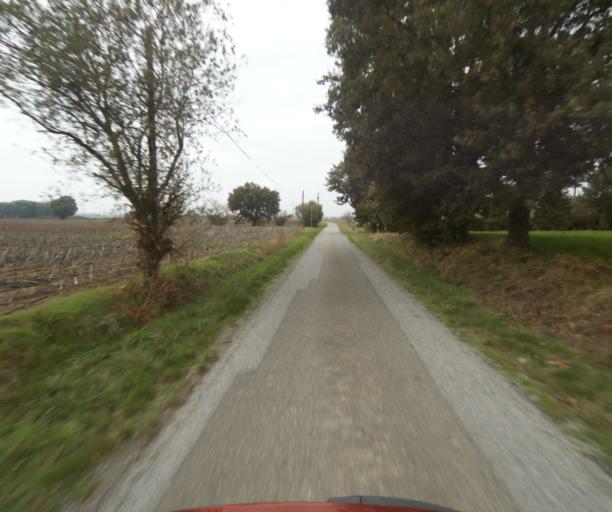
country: FR
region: Midi-Pyrenees
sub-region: Departement du Tarn-et-Garonne
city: Verdun-sur-Garonne
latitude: 43.8424
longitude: 1.1817
